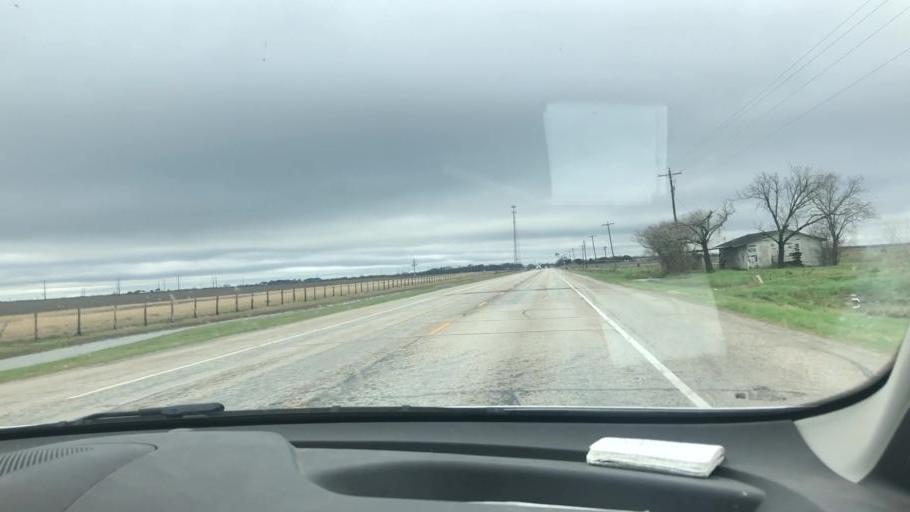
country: US
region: Texas
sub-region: Wharton County
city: Wharton
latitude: 29.2386
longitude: -96.0393
